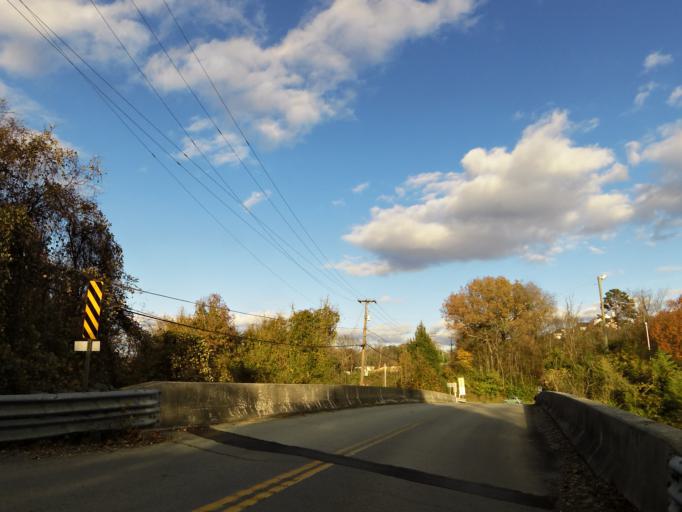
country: US
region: Tennessee
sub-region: Blount County
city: Eagleton Village
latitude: 35.8760
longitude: -83.9607
